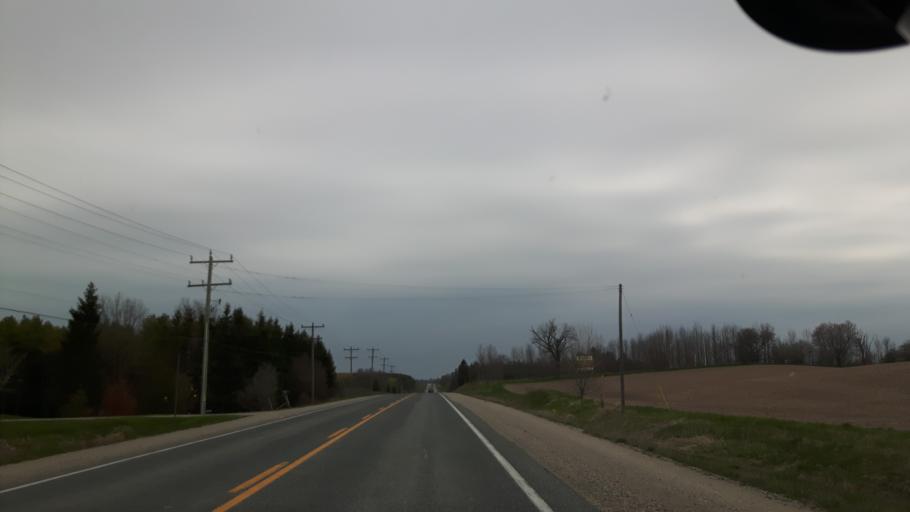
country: CA
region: Ontario
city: Goderich
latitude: 43.6635
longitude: -81.6195
